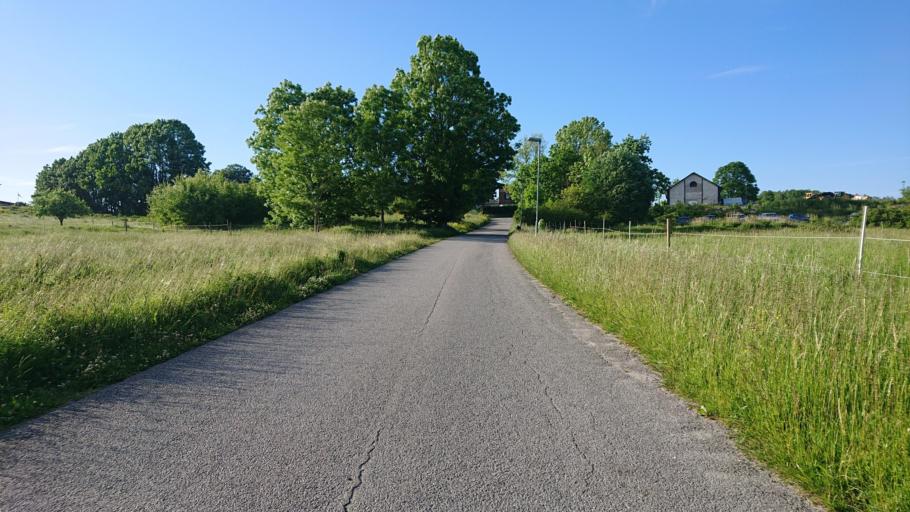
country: SE
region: Stockholm
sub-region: Osterakers Kommun
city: Akersberga
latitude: 59.4987
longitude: 18.2932
